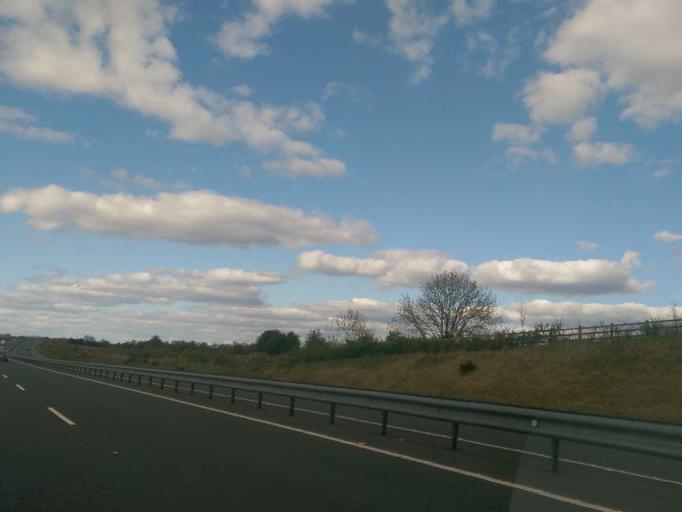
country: IE
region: Leinster
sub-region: An Iarmhi
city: Athlone
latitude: 53.3898
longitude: -8.0500
